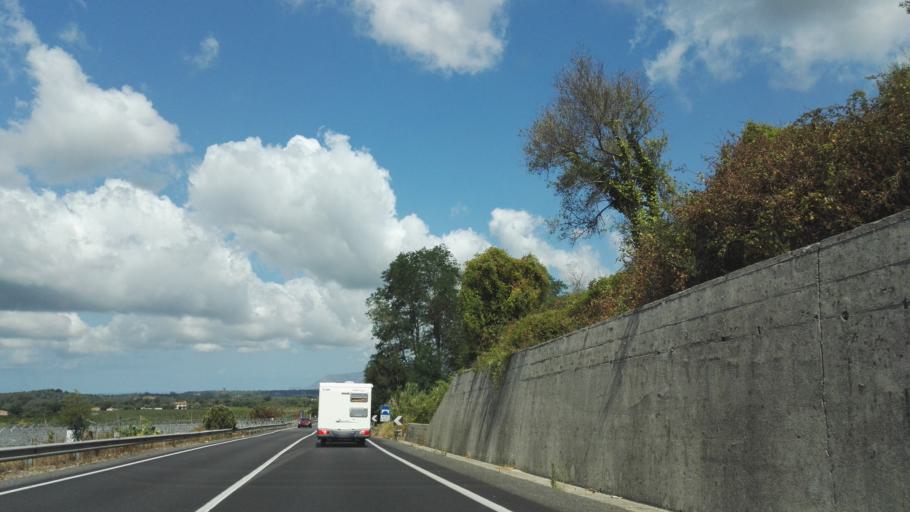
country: IT
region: Calabria
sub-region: Provincia di Reggio Calabria
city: Melicucco
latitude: 38.4401
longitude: 16.0436
